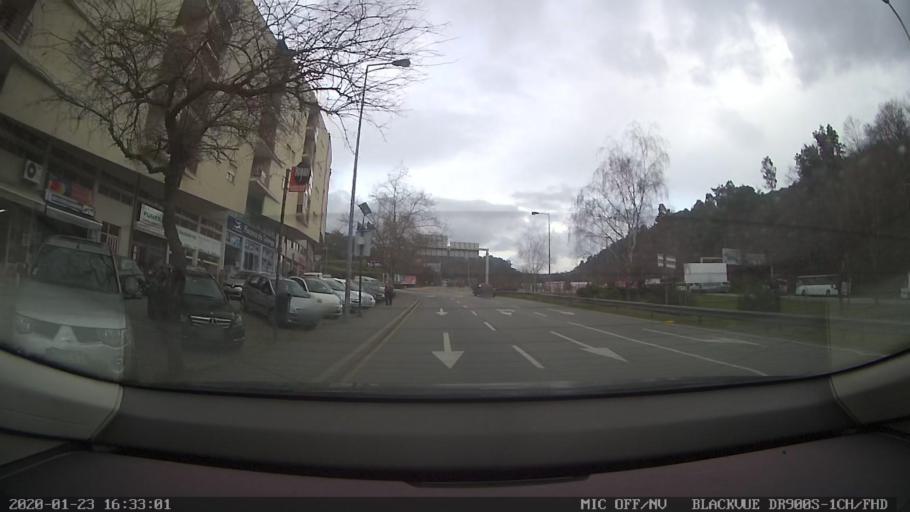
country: PT
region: Porto
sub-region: Amarante
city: Amarante
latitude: 41.2654
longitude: -8.0694
